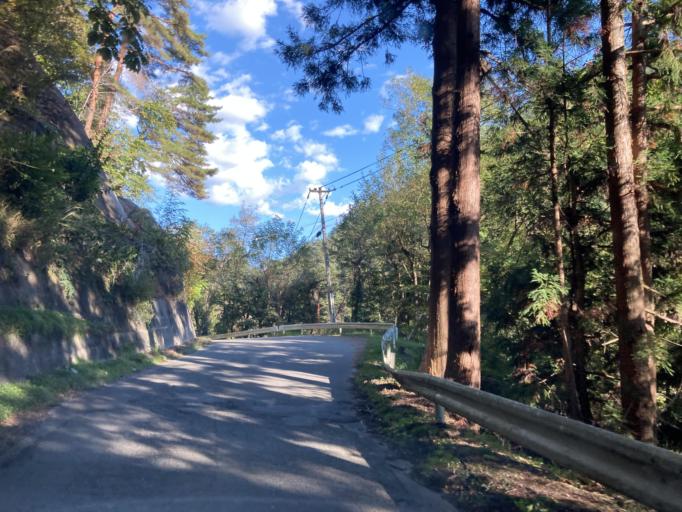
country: JP
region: Nagano
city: Omachi
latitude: 36.4523
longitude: 137.9700
